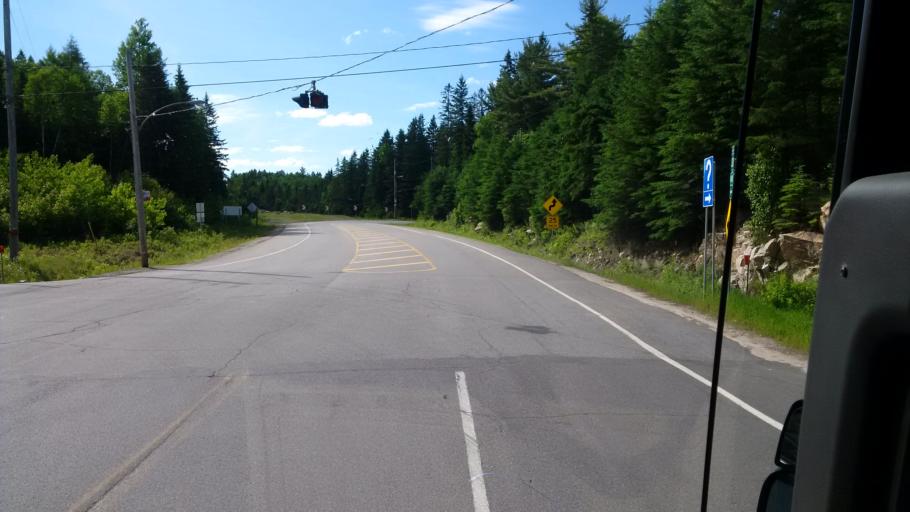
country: CA
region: Quebec
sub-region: Laurentides
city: Riviere-Rouge
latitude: 46.4349
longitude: -74.8994
